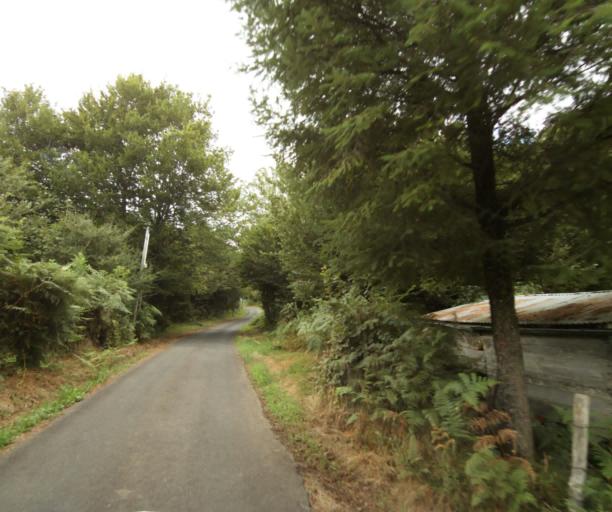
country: FR
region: Limousin
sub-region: Departement de la Correze
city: Sainte-Fortunade
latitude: 45.1756
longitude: 1.8170
